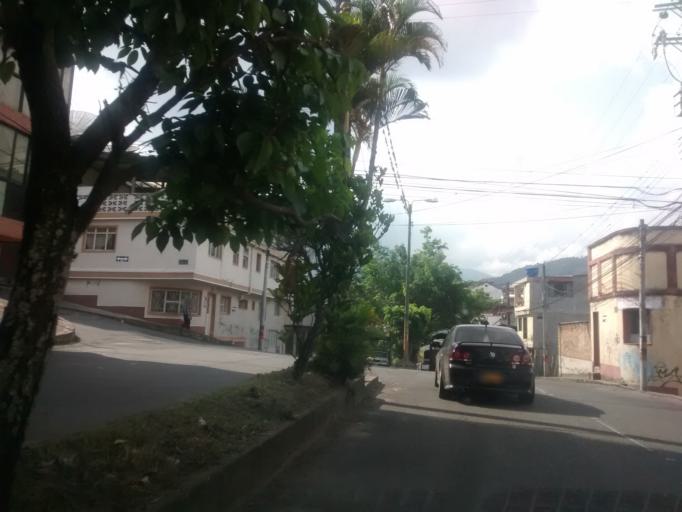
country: CO
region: Tolima
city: Ibague
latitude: 4.4469
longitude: -75.2374
